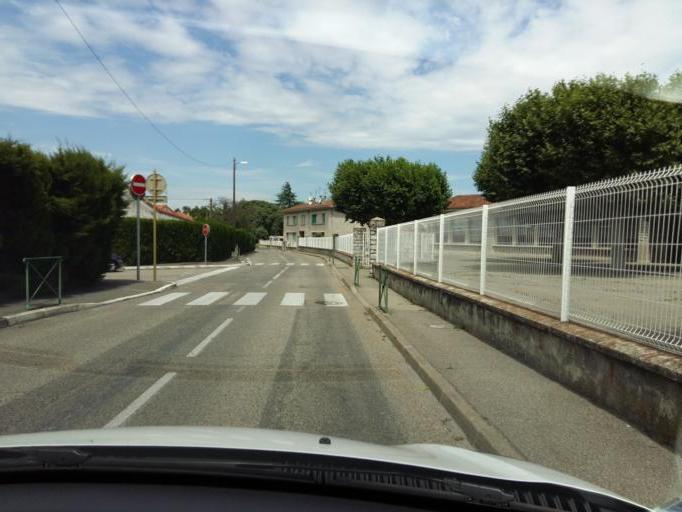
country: FR
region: Provence-Alpes-Cote d'Azur
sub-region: Departement du Vaucluse
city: Bollene
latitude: 44.3014
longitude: 4.7524
